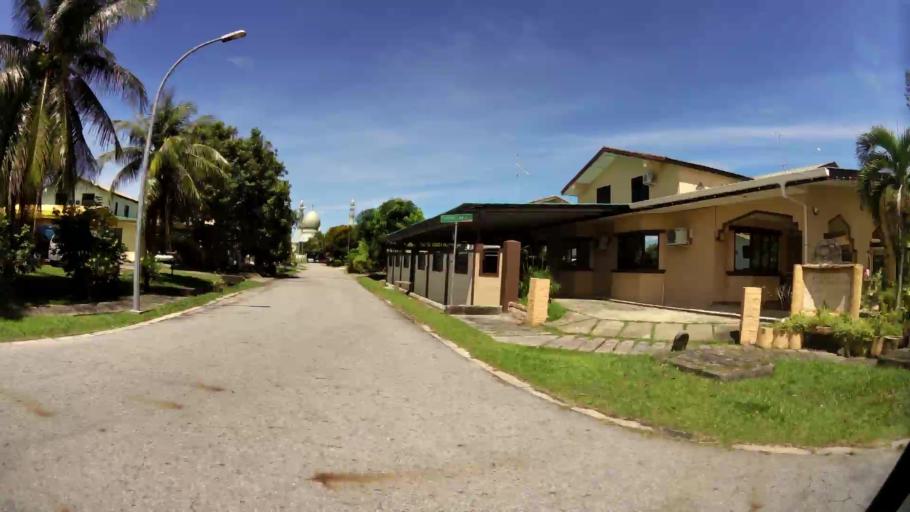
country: BN
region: Belait
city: Kuala Belait
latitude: 4.5858
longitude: 114.2287
